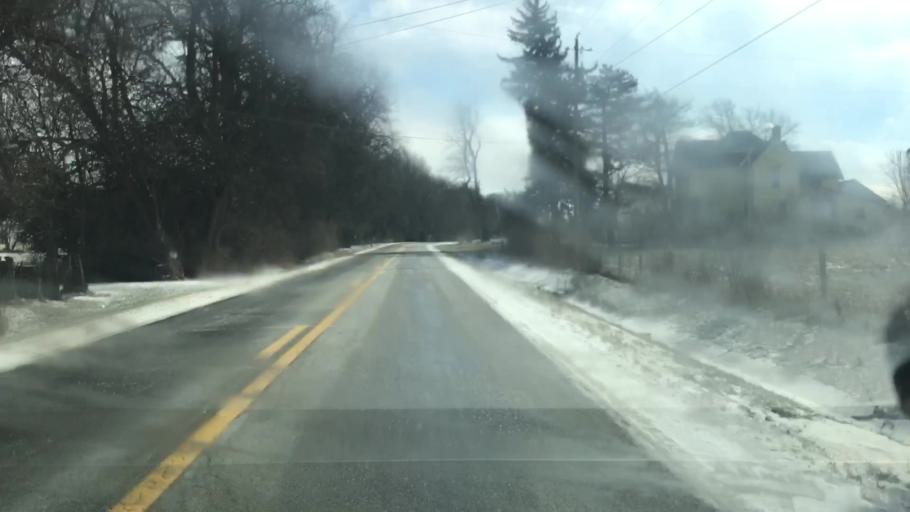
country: US
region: Ohio
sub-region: Franklin County
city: Hilliard
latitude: 40.0211
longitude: -83.2189
